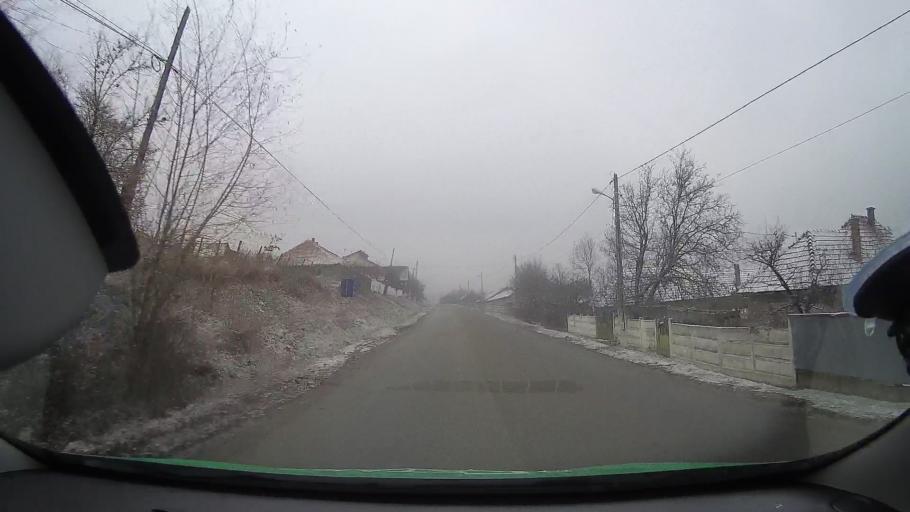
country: RO
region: Alba
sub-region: Comuna Noslac
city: Noslac
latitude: 46.3454
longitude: 23.9412
